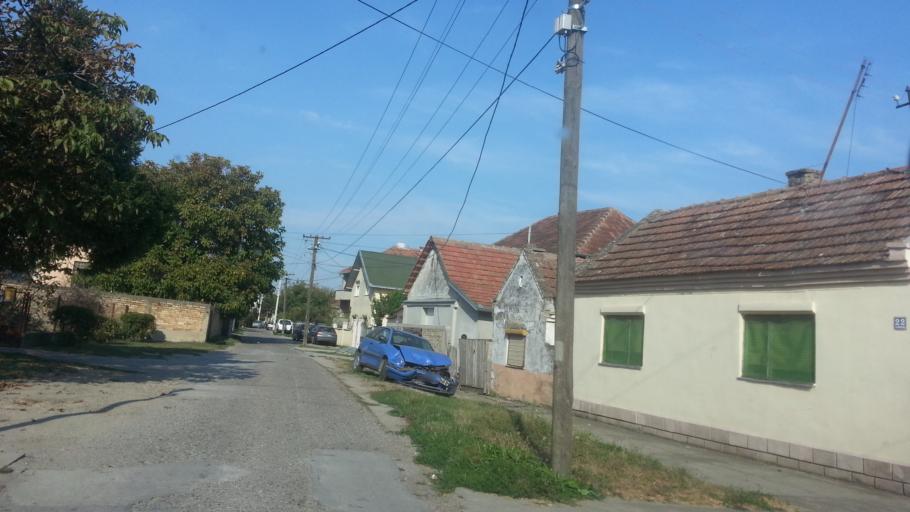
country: RS
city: Stari Banovci
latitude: 44.9898
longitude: 20.2835
